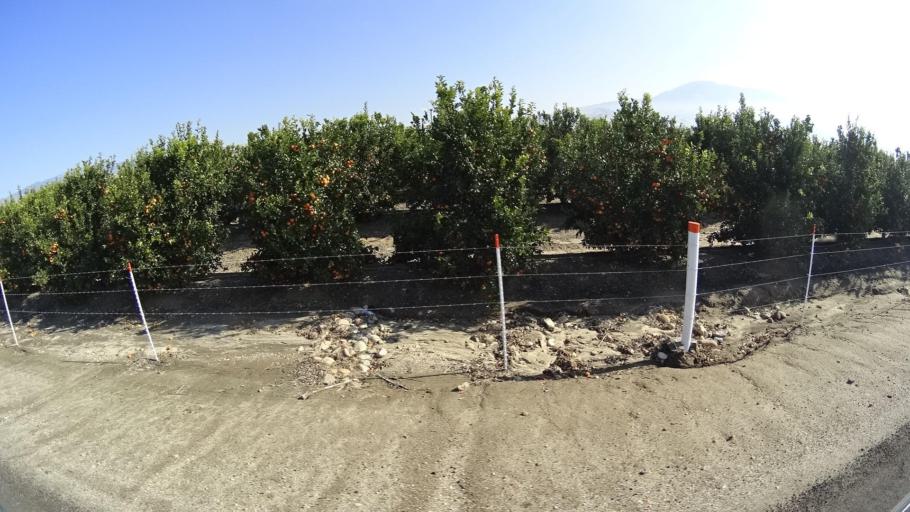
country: US
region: California
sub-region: Kern County
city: Arvin
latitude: 35.2775
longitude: -118.7707
